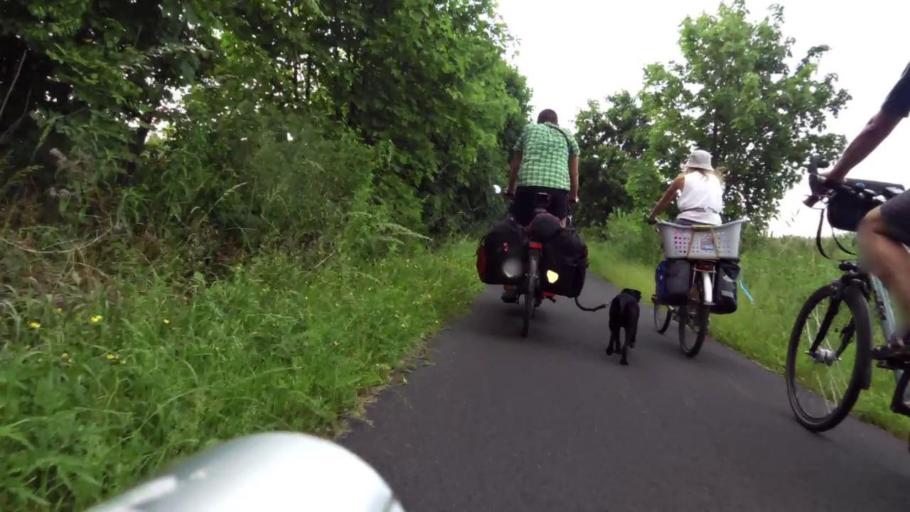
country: PL
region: Kujawsko-Pomorskie
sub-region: Powiat torunski
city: Lubianka
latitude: 53.0985
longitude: 18.5299
